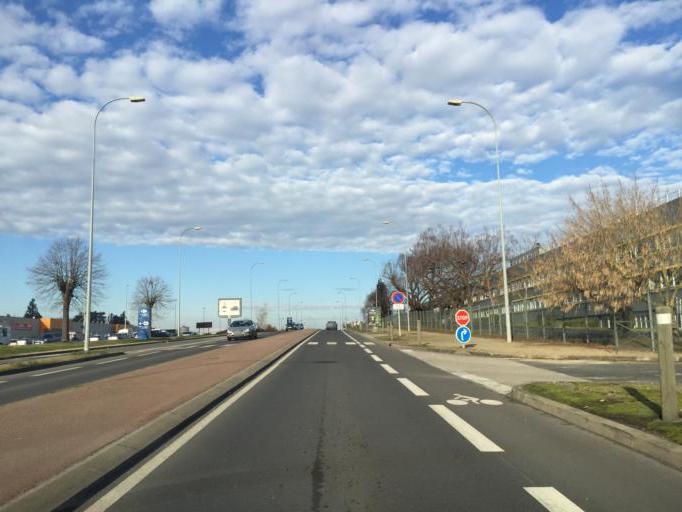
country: FR
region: Auvergne
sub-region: Departement de l'Allier
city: Toulon-sur-Allier
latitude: 46.5385
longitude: 3.3457
